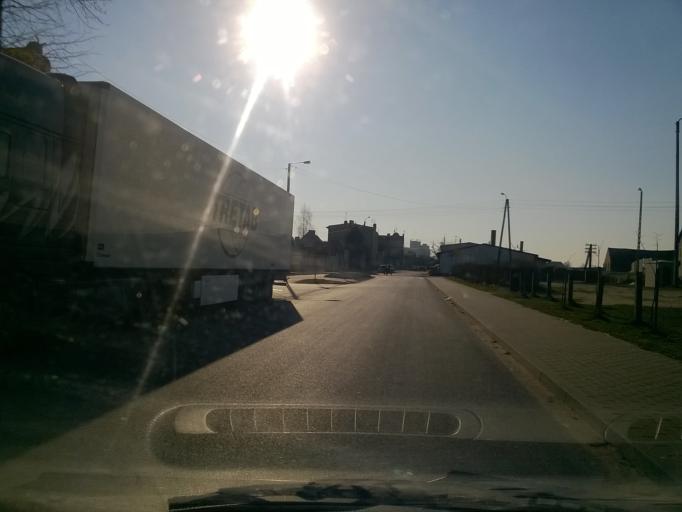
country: PL
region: Greater Poland Voivodeship
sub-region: Powiat wagrowiecki
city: Golancz
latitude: 52.9464
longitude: 17.3023
